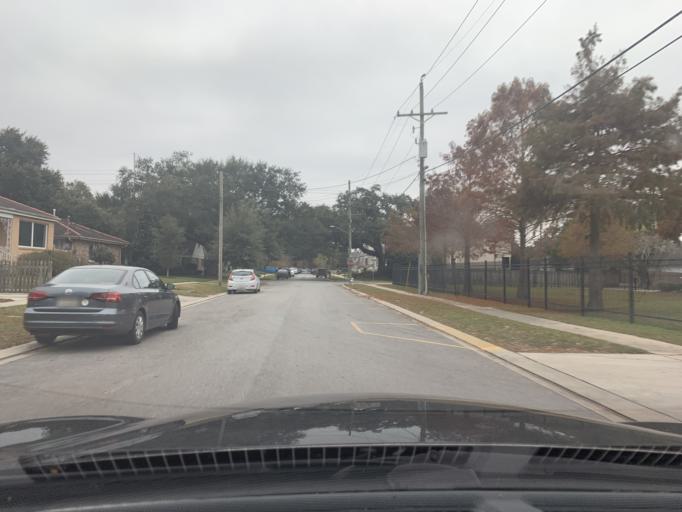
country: US
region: Louisiana
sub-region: Jefferson Parish
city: Metairie
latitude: 30.0189
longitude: -90.1088
